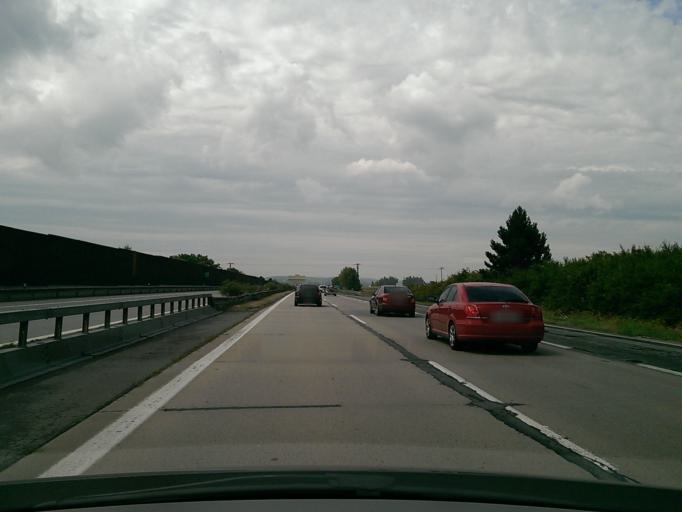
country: CZ
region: Vysocina
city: Merin
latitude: 49.3979
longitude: 15.8784
